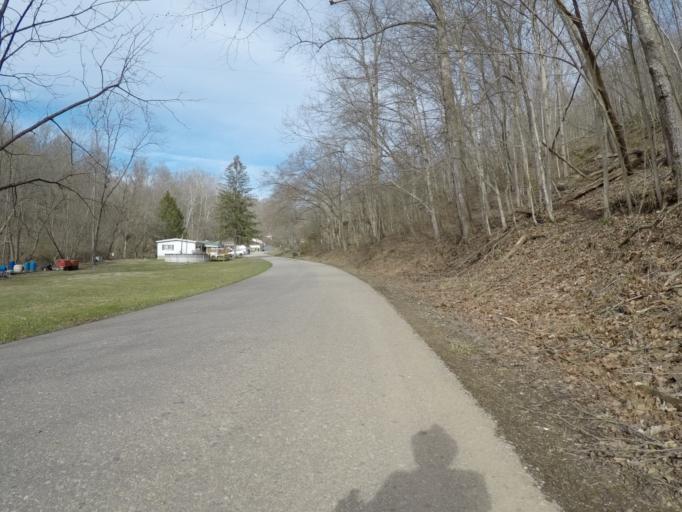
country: US
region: West Virginia
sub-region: Wayne County
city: Lavalette
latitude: 38.3547
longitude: -82.4898
